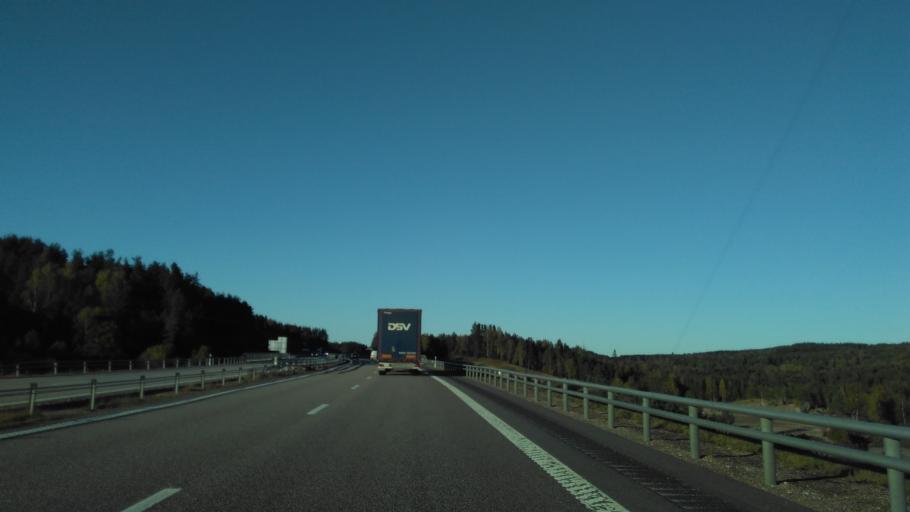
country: SE
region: Vaestra Goetaland
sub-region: Boras Kommun
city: Dalsjofors
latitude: 57.7649
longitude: 13.1113
